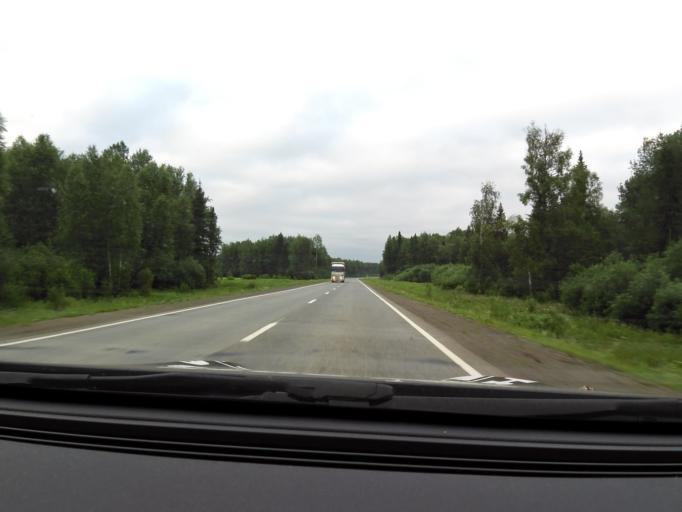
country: RU
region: Perm
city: Zyukayka
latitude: 58.3693
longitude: 54.6641
